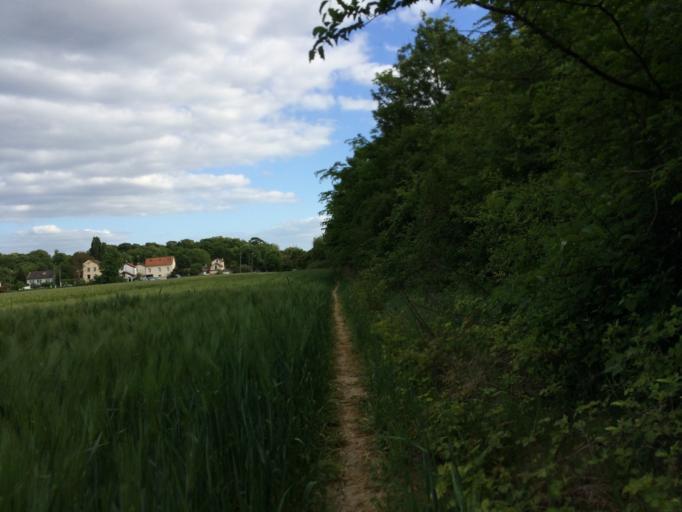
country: FR
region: Ile-de-France
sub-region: Departement de l'Essonne
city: Ris-Orangis
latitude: 48.6639
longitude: 2.4140
